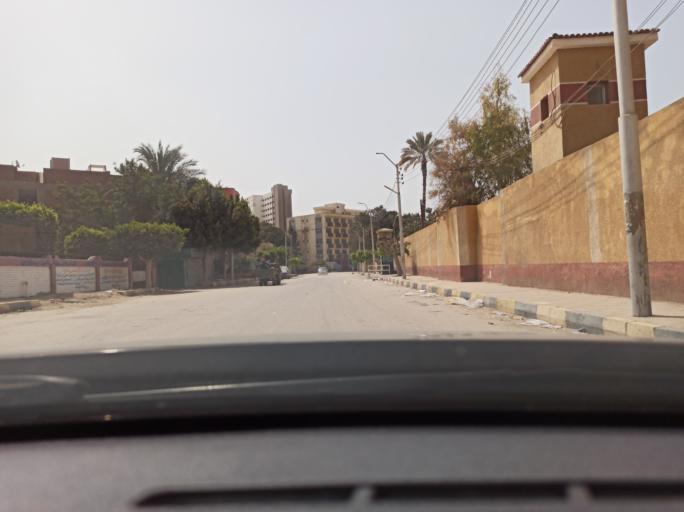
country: EG
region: Muhafazat Bani Suwayf
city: Bani Suwayf
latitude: 29.0839
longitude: 31.0933
